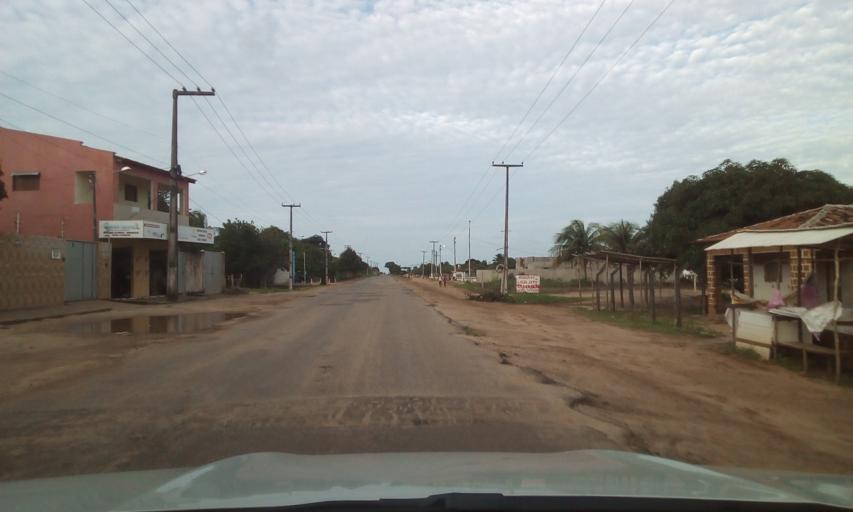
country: BR
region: Paraiba
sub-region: Conde
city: Conde
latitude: -7.2675
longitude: -34.8465
